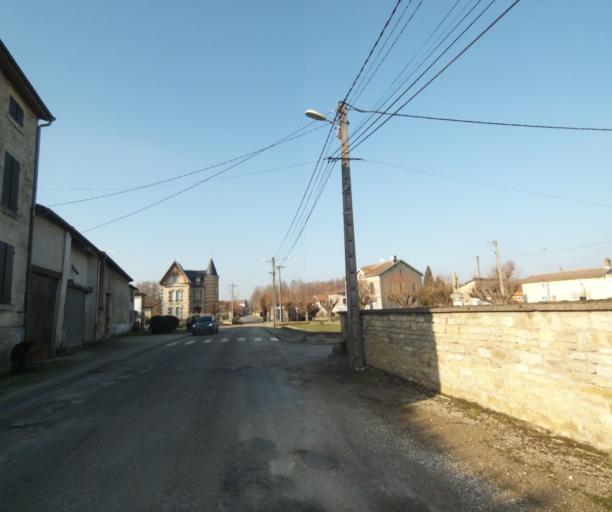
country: FR
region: Champagne-Ardenne
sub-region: Departement de la Haute-Marne
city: Wassy
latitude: 48.4711
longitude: 4.9701
